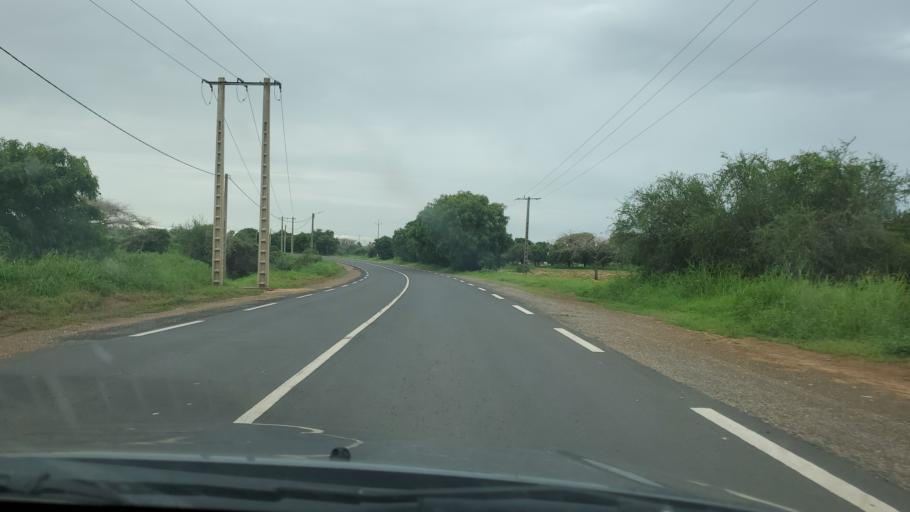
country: SN
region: Thies
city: Kayar
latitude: 15.1096
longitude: -16.9143
